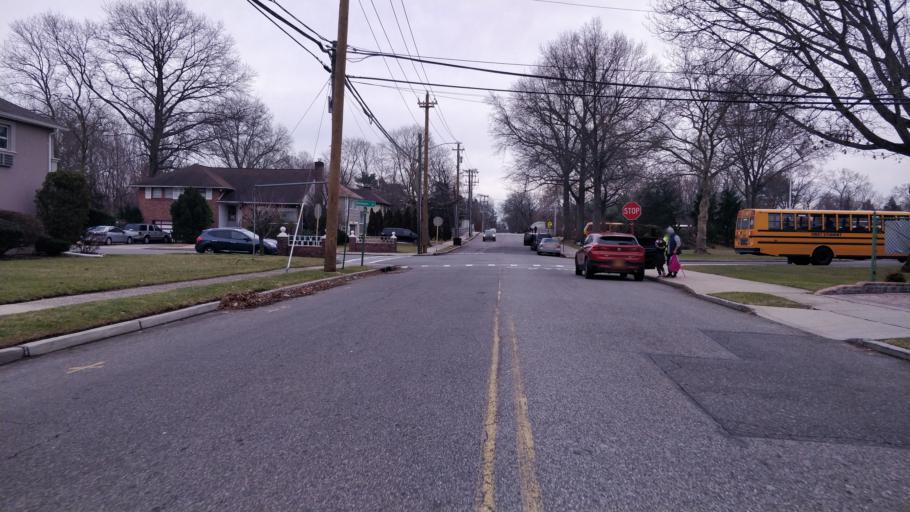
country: US
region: New York
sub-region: Nassau County
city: New Cassel
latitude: 40.7682
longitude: -73.5770
